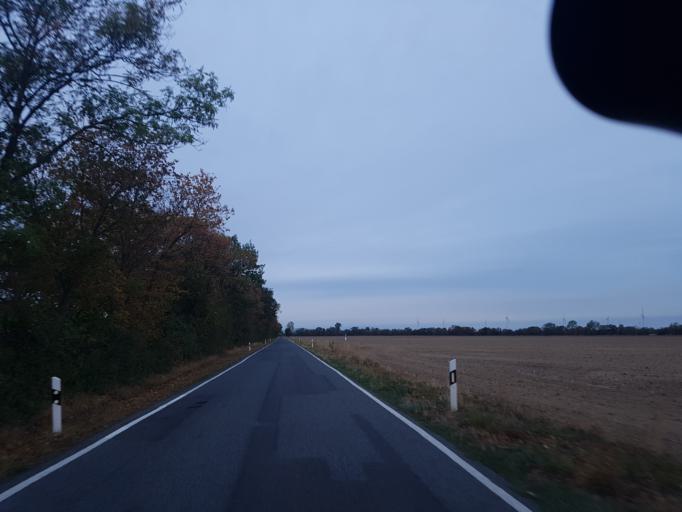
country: DE
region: Brandenburg
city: Muhlberg
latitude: 51.4973
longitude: 13.2526
